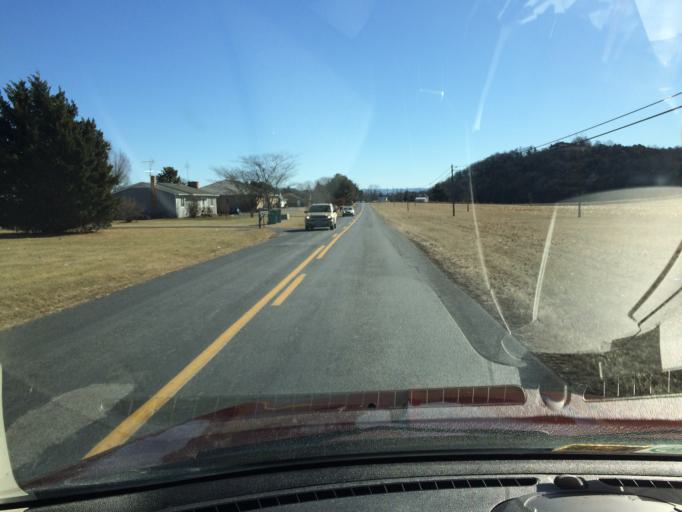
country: US
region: Virginia
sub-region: Rockingham County
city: Bridgewater
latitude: 38.3607
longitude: -78.9591
